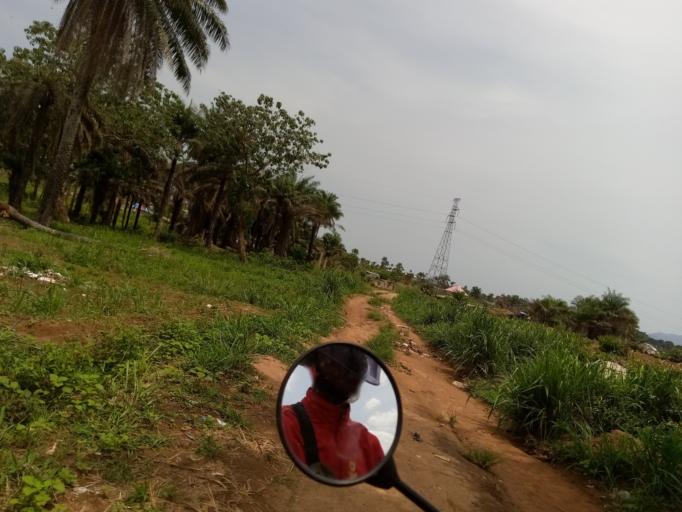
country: SL
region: Western Area
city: Waterloo
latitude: 8.3312
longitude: -13.0221
